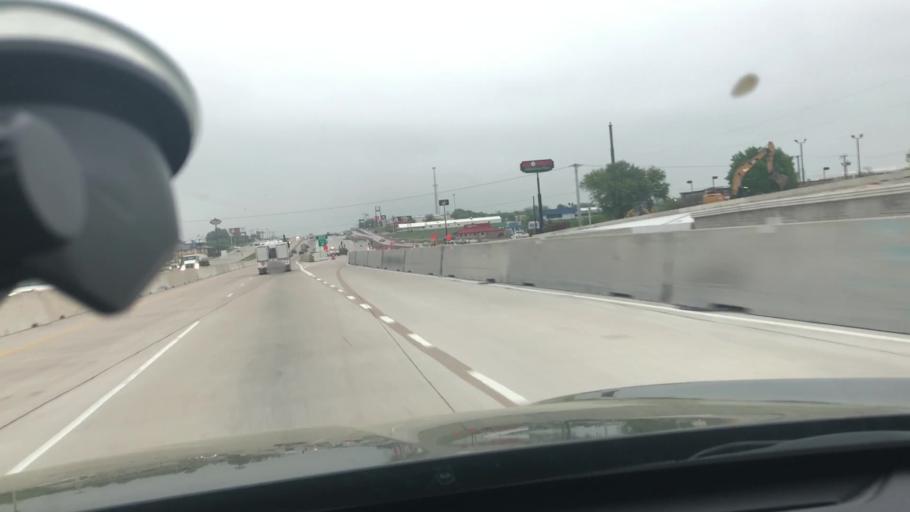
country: US
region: Texas
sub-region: Bell County
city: Temple
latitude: 31.1039
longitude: -97.3591
